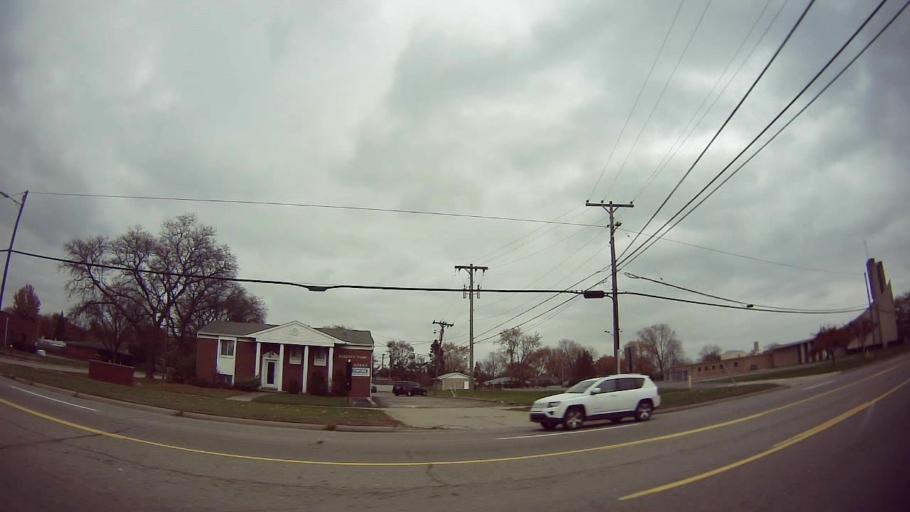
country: US
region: Michigan
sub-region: Macomb County
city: Center Line
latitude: 42.4939
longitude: -83.0067
